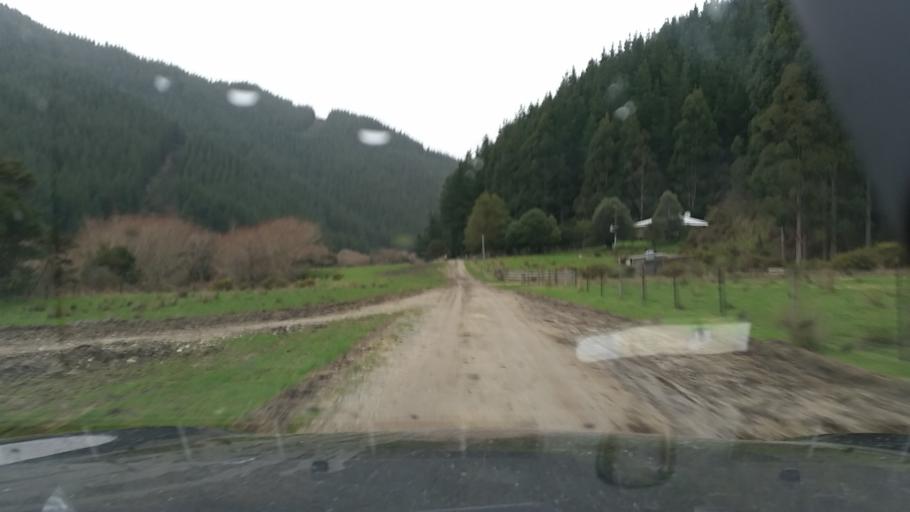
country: NZ
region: Marlborough
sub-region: Marlborough District
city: Blenheim
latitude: -41.3915
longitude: 173.8494
